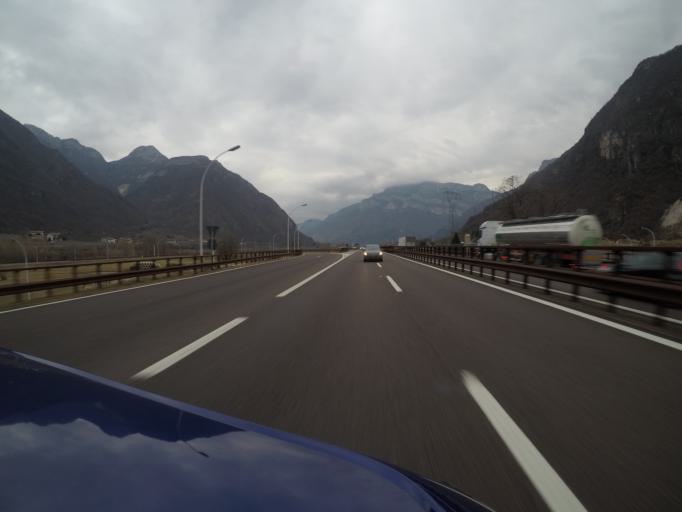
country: IT
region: Trentino-Alto Adige
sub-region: Provincia di Trento
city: Sabbionara
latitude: 45.7461
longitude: 10.9810
